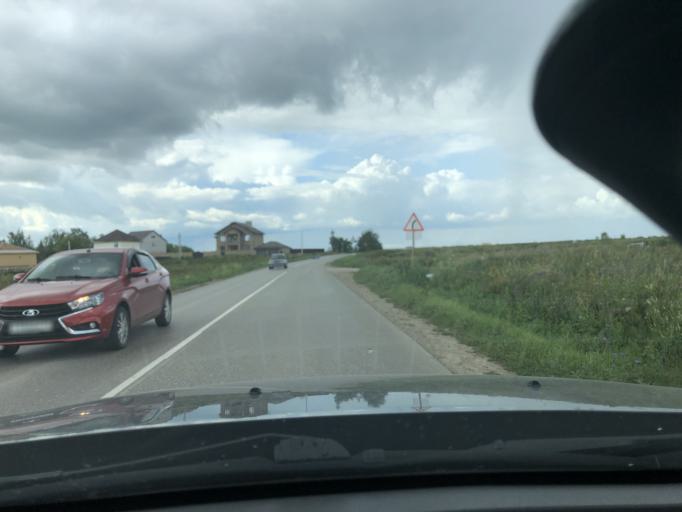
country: RU
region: Tula
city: Kamenetskiy
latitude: 54.0114
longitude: 38.2520
